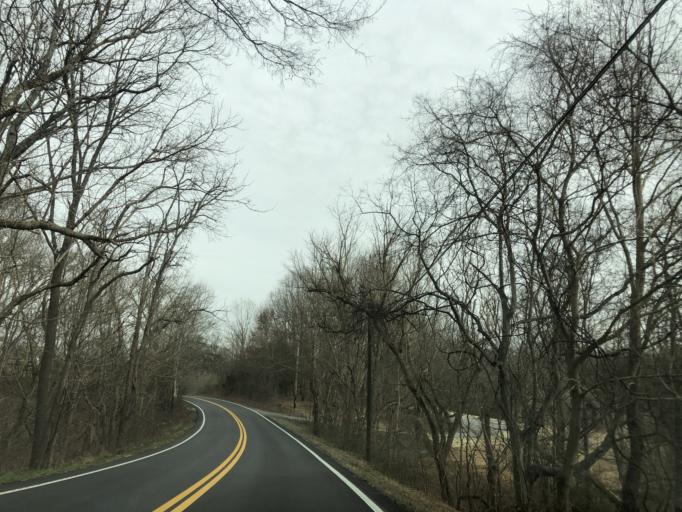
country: US
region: Tennessee
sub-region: Sumner County
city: White House
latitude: 36.4765
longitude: -86.7291
